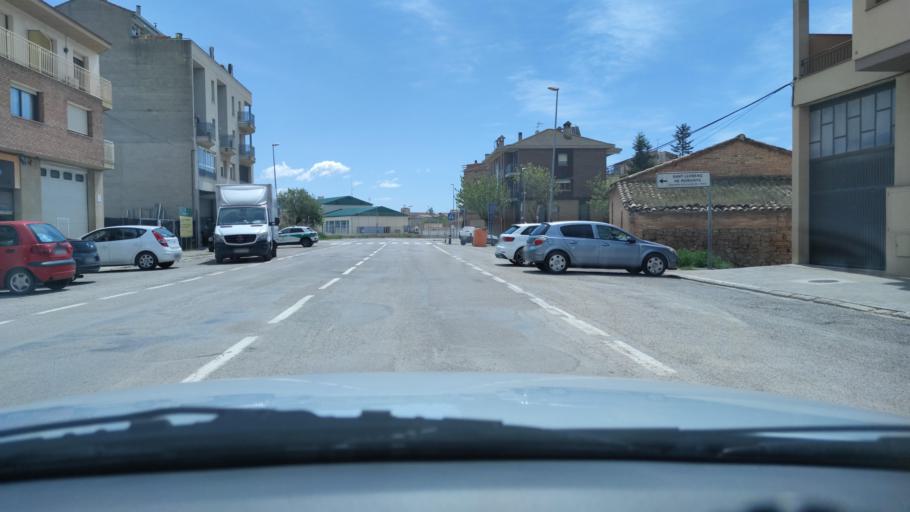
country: ES
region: Catalonia
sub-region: Provincia de Lleida
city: Solsona
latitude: 41.9991
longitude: 1.5201
